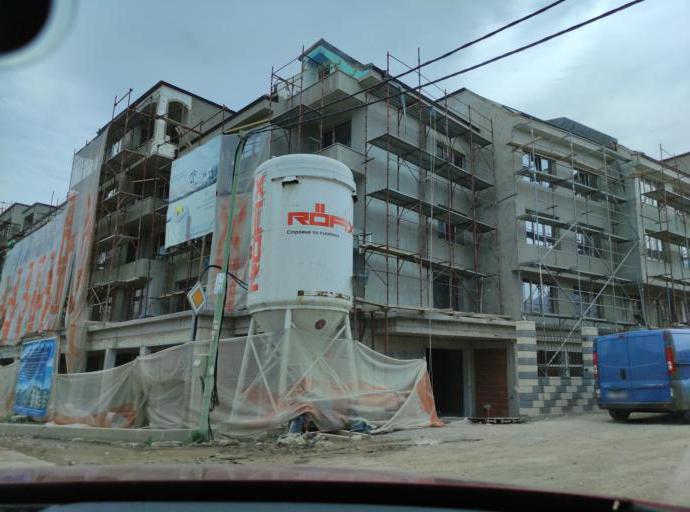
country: BG
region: Sofia-Capital
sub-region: Stolichna Obshtina
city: Sofia
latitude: 42.6365
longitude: 23.3407
